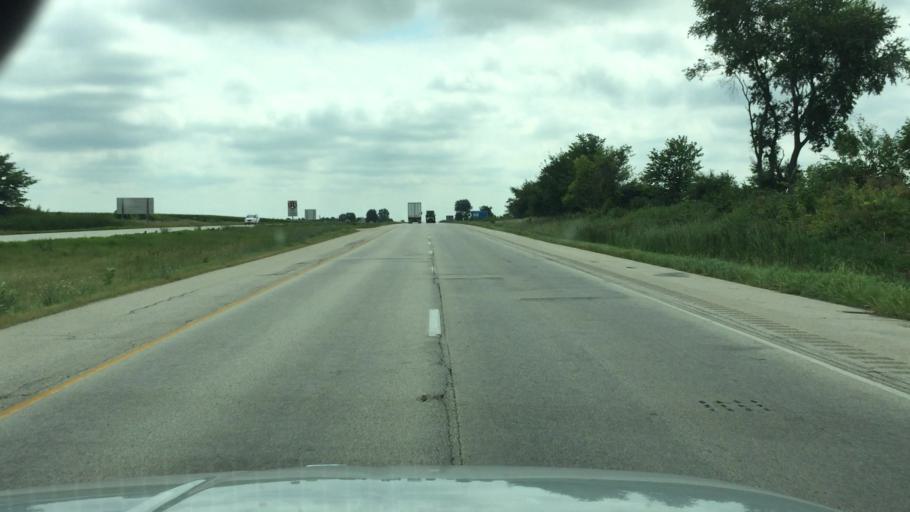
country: US
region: Illinois
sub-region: Knox County
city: Galesburg
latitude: 40.9374
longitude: -90.3286
